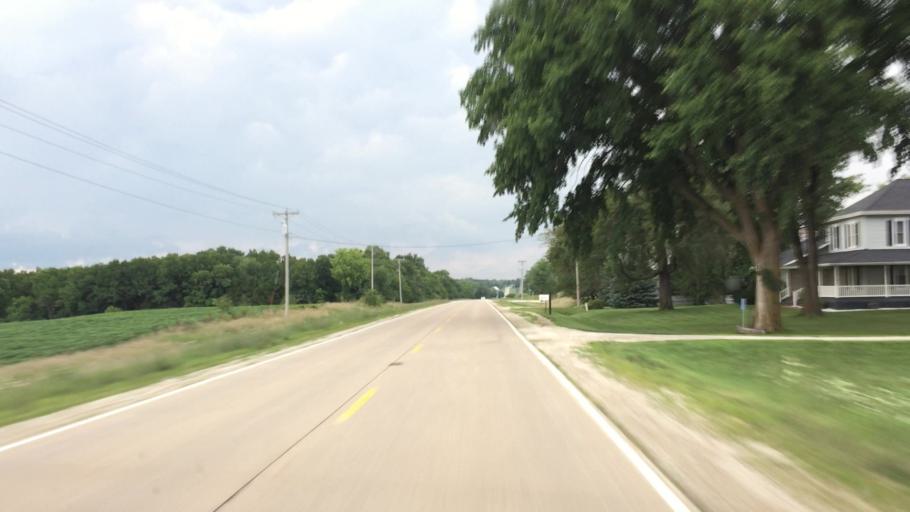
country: US
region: Iowa
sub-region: Lee County
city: Fort Madison
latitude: 40.7088
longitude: -91.3300
